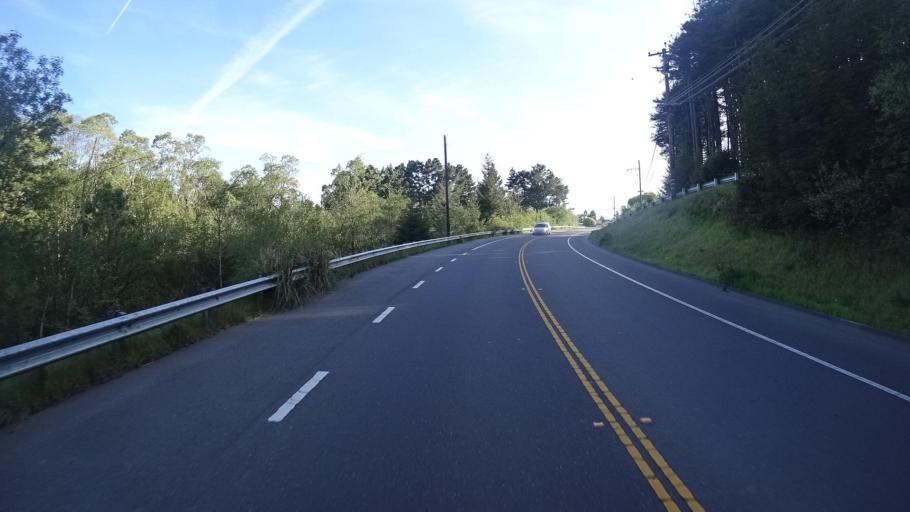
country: US
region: California
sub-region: Humboldt County
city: Bayview
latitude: 40.7699
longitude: -124.1751
